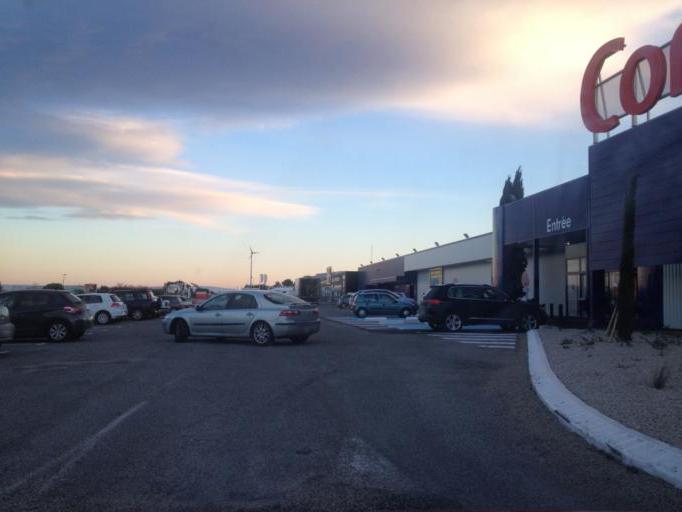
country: FR
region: Provence-Alpes-Cote d'Azur
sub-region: Departement du Vaucluse
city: Orange
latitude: 44.1137
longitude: 4.8431
